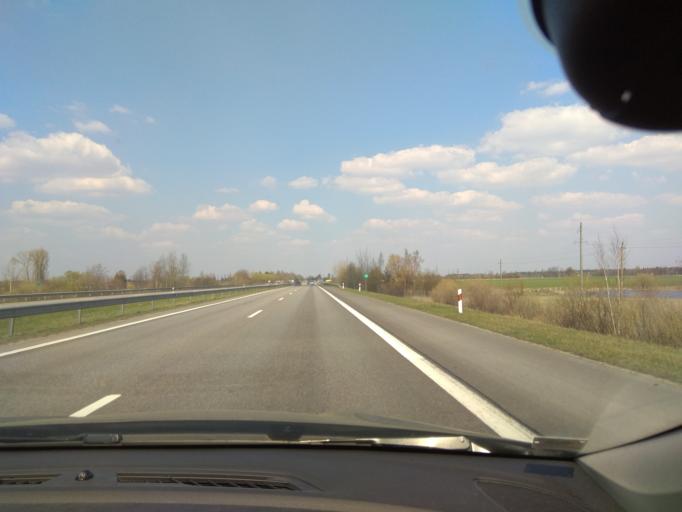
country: LT
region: Kauno apskritis
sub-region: Kaunas
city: Sargenai
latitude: 55.0674
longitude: 23.8160
